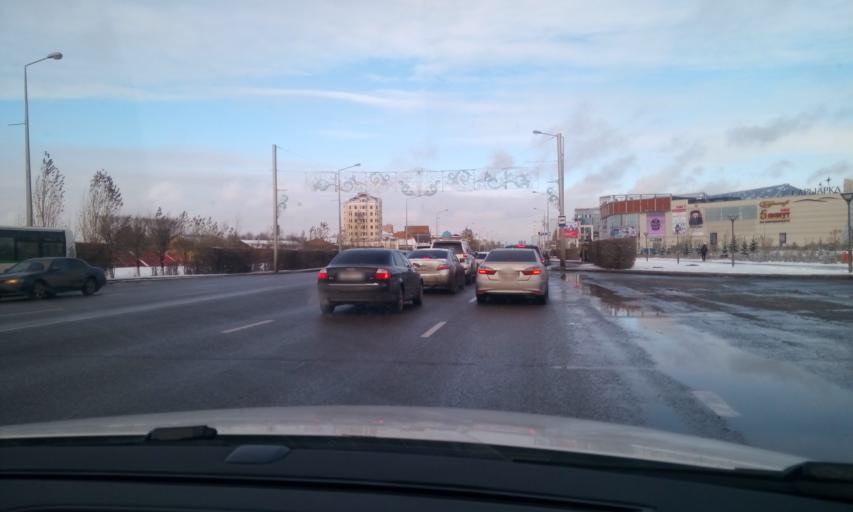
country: KZ
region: Astana Qalasy
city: Astana
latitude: 51.1355
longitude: 71.4081
